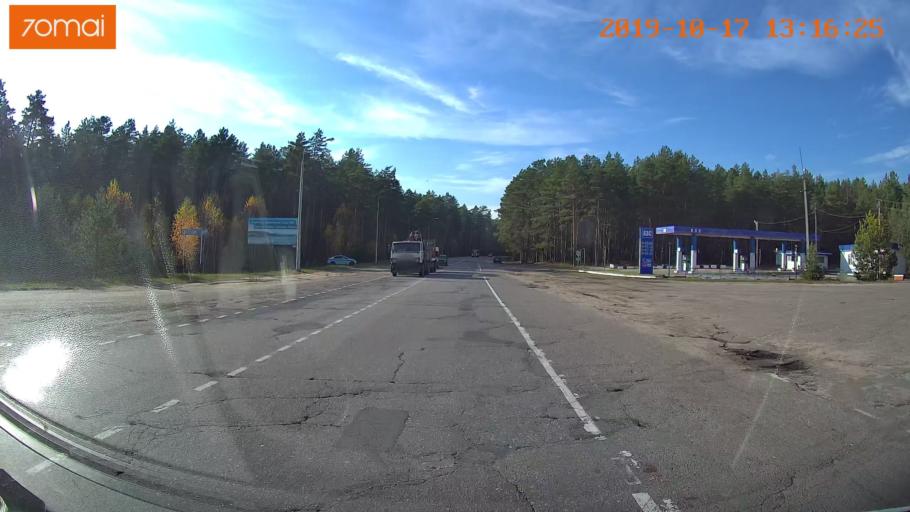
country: RU
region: Rjazan
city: Gus'-Zheleznyy
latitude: 55.0494
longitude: 41.1407
